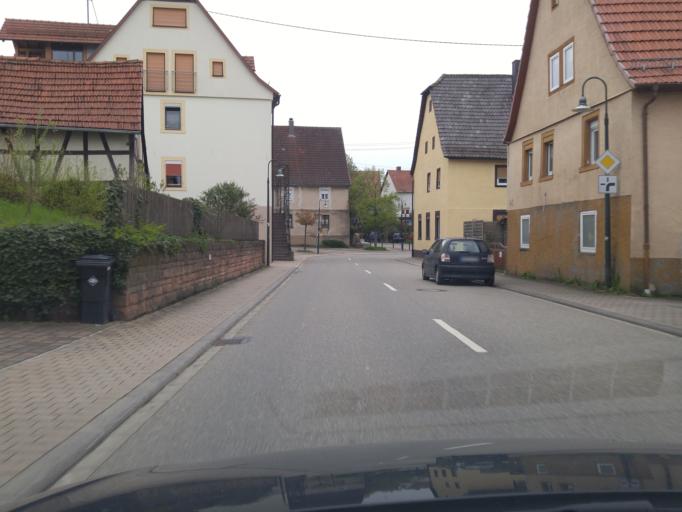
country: DE
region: Baden-Wuerttemberg
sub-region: Karlsruhe Region
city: Aglasterhausen
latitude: 49.3425
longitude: 9.0237
